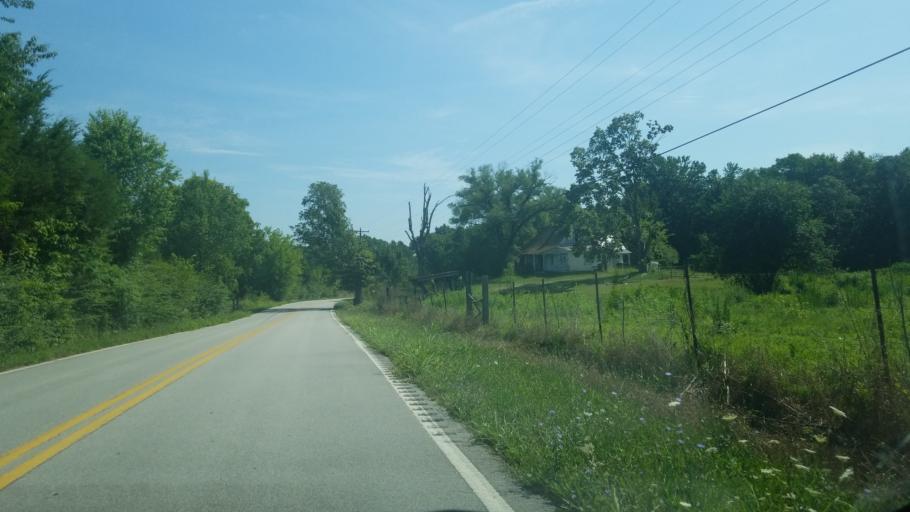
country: US
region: Tennessee
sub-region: Hamilton County
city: Sale Creek
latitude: 35.3083
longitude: -85.0339
